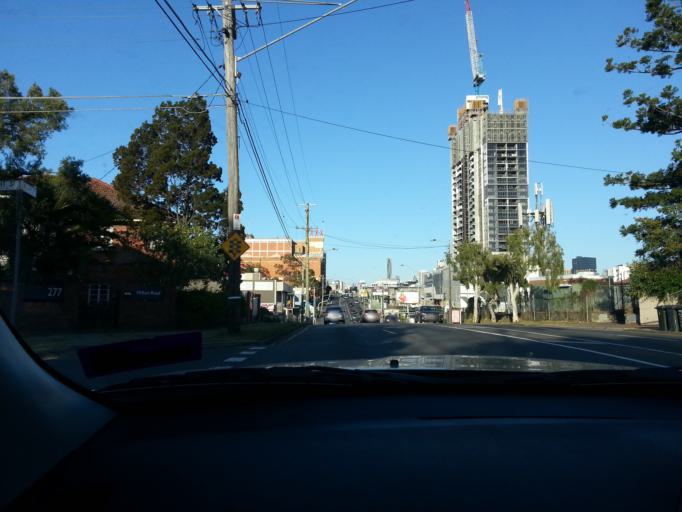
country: AU
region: Queensland
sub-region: Brisbane
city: Milton
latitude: -27.4696
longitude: 153.0022
